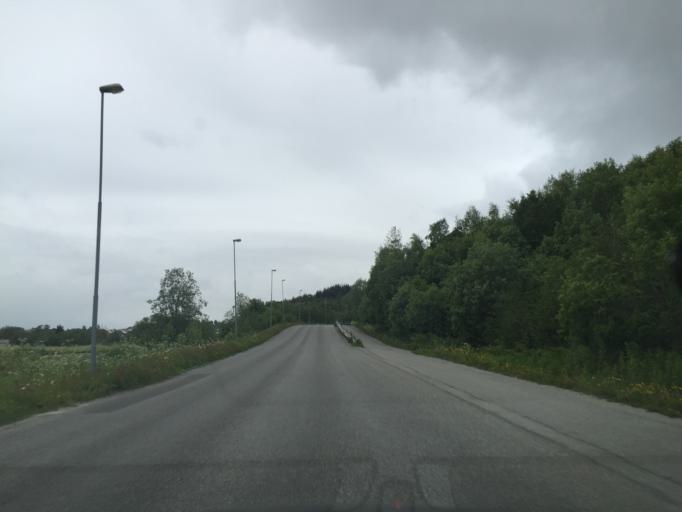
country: NO
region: Nordland
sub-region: Bodo
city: Lopsmarka
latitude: 67.2884
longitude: 14.5813
